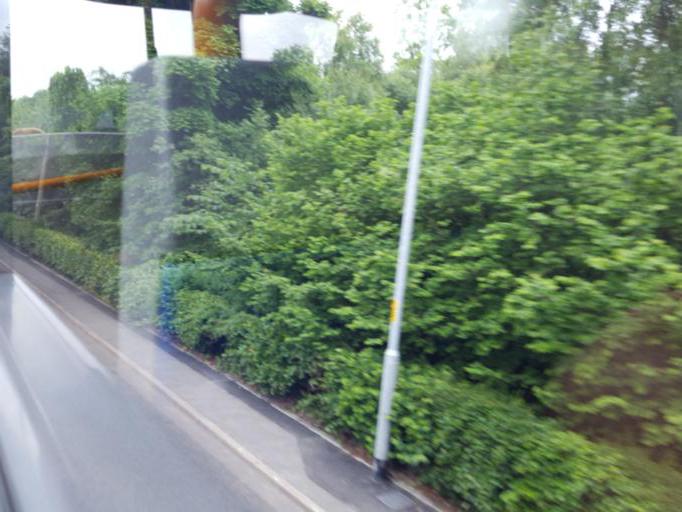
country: GB
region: England
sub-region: Cumbria
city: Keswick
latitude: 54.5984
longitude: -3.1181
